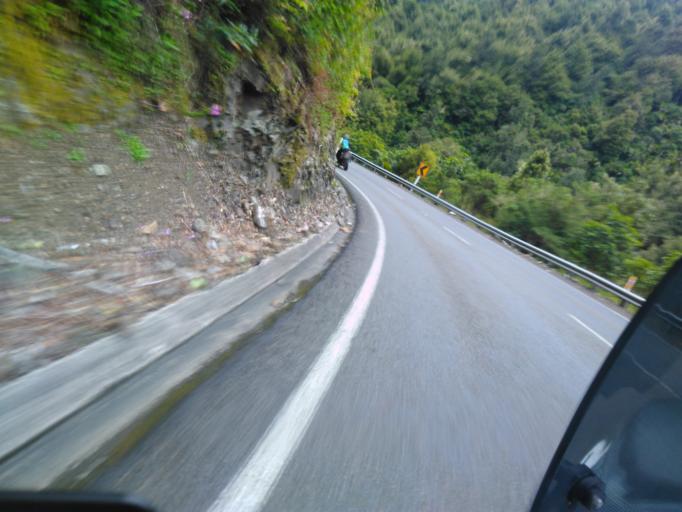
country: NZ
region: Bay of Plenty
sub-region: Opotiki District
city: Opotiki
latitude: -38.2714
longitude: 177.3206
